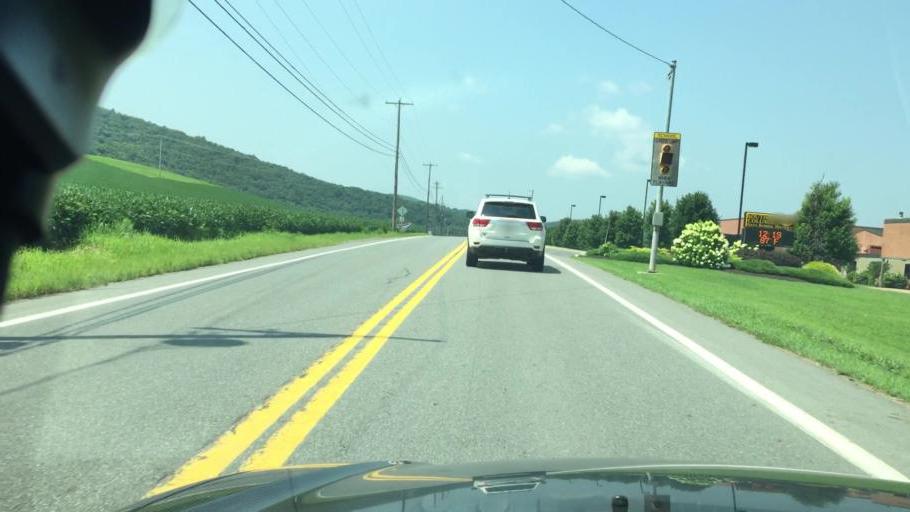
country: US
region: Pennsylvania
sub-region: Columbia County
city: Catawissa
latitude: 40.9038
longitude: -76.4955
